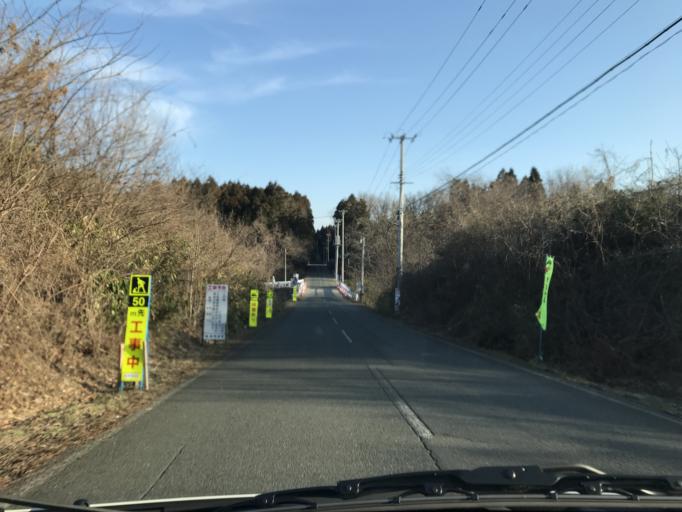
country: JP
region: Iwate
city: Kitakami
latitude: 39.2233
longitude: 141.1037
